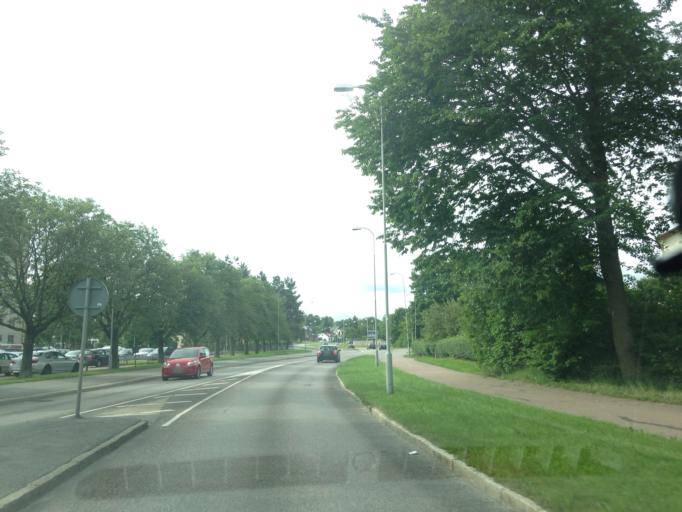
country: SE
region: Vaestra Goetaland
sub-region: Goteborg
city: Goeteborg
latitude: 57.7329
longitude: 11.9743
